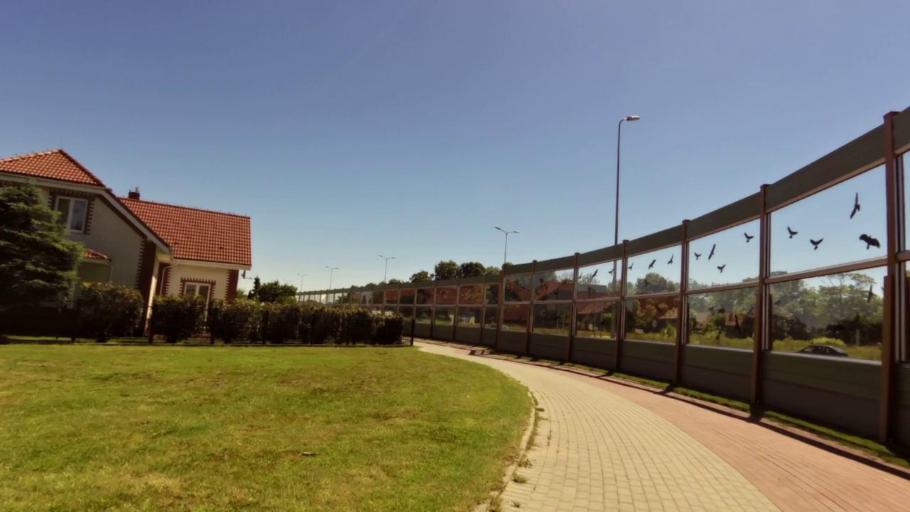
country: PL
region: West Pomeranian Voivodeship
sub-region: Powiat kolobrzeski
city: Kolobrzeg
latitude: 54.1638
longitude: 15.5500
